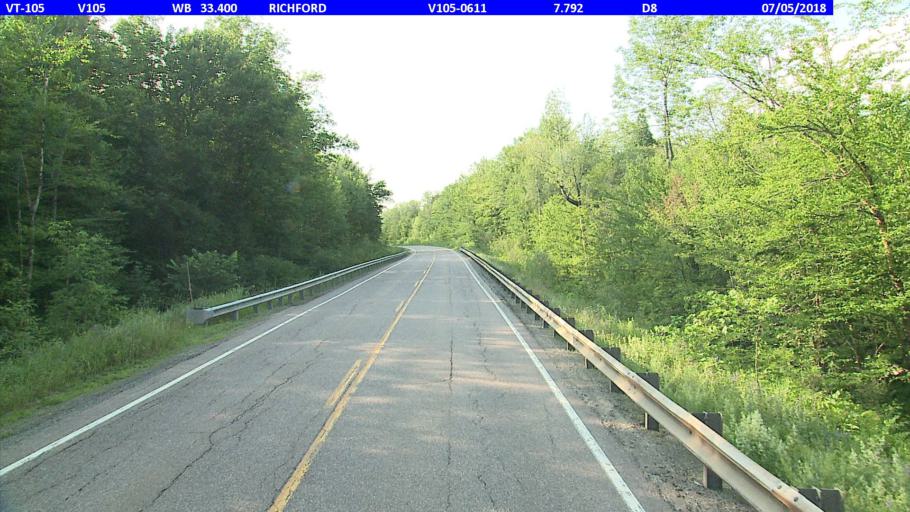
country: US
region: Vermont
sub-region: Franklin County
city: Richford
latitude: 44.9982
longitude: -72.5721
